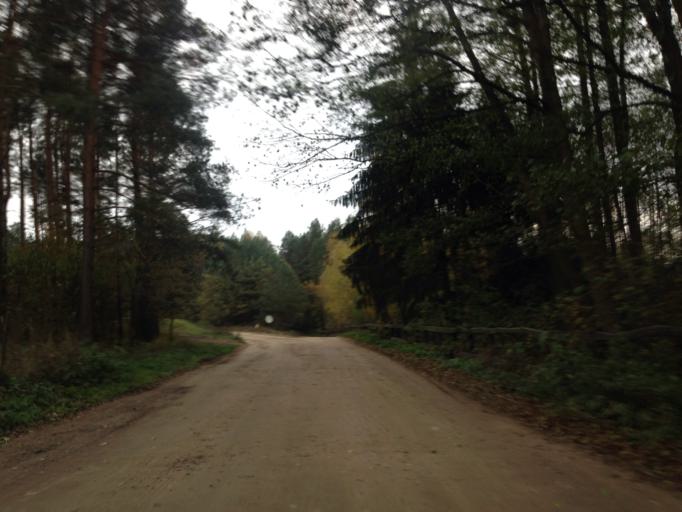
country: PL
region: Kujawsko-Pomorskie
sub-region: Powiat brodnicki
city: Brzozie
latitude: 53.3074
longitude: 19.5589
